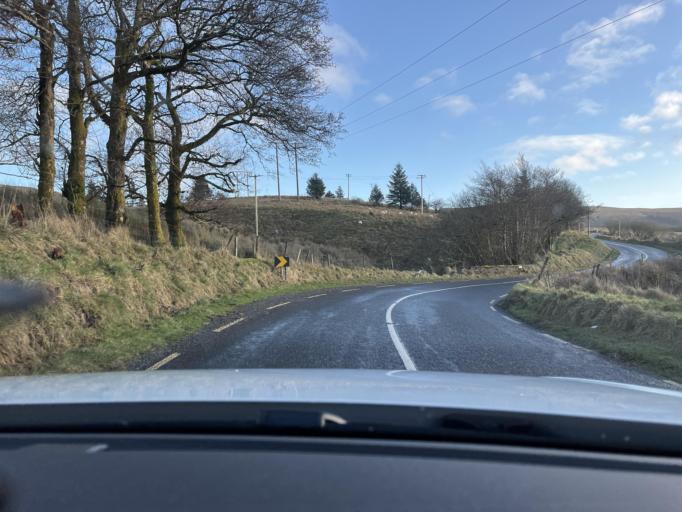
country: GB
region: Northern Ireland
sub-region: Fermanagh District
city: Enniskillen
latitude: 54.1767
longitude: -7.8518
